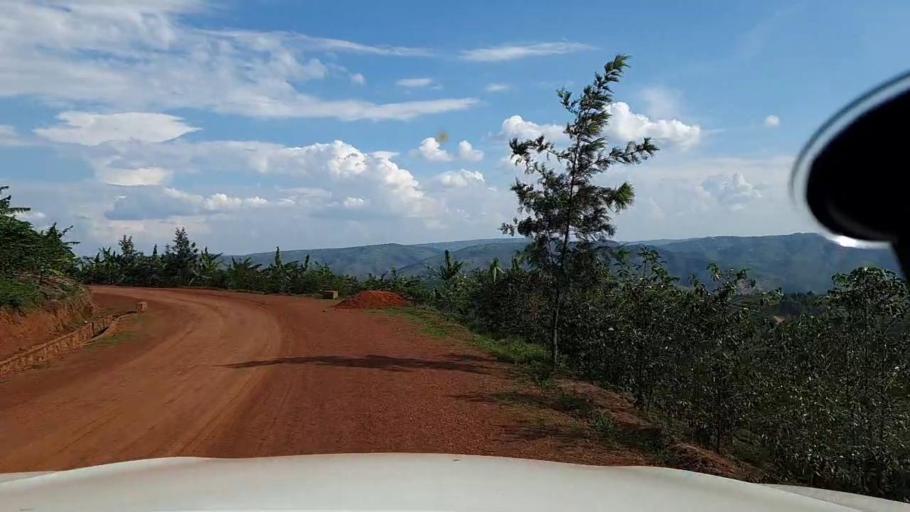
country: RW
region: Kigali
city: Kigali
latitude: -1.8369
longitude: 29.8469
